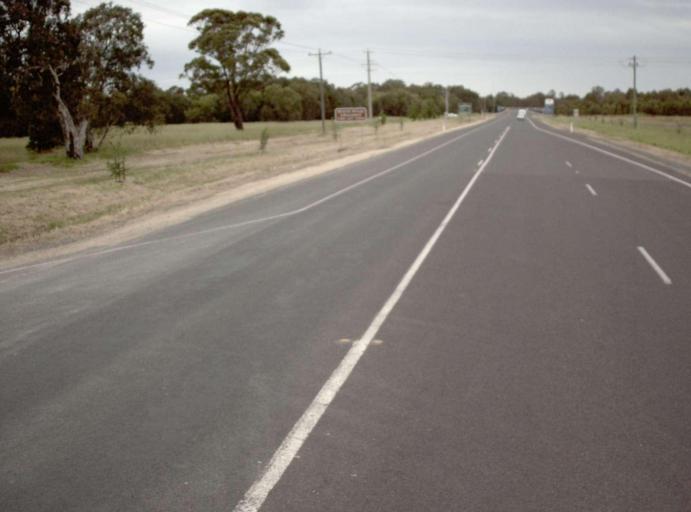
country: AU
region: Victoria
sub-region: Wellington
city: Sale
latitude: -38.1204
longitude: 147.0684
